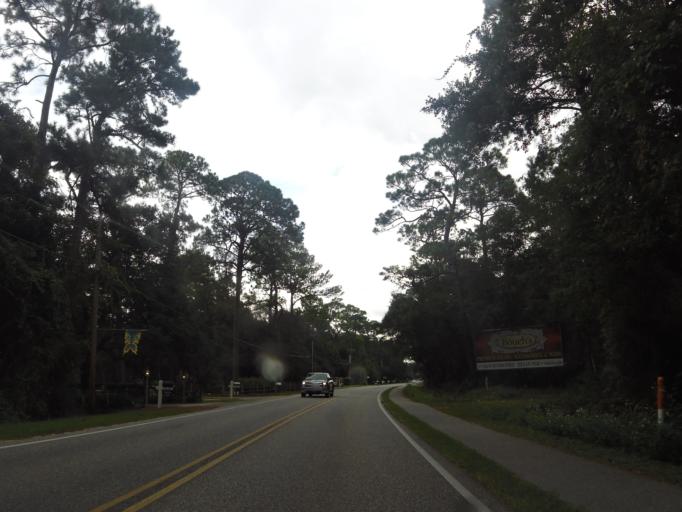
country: US
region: Alabama
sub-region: Baldwin County
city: Fairhope
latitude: 30.5041
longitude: -87.9218
